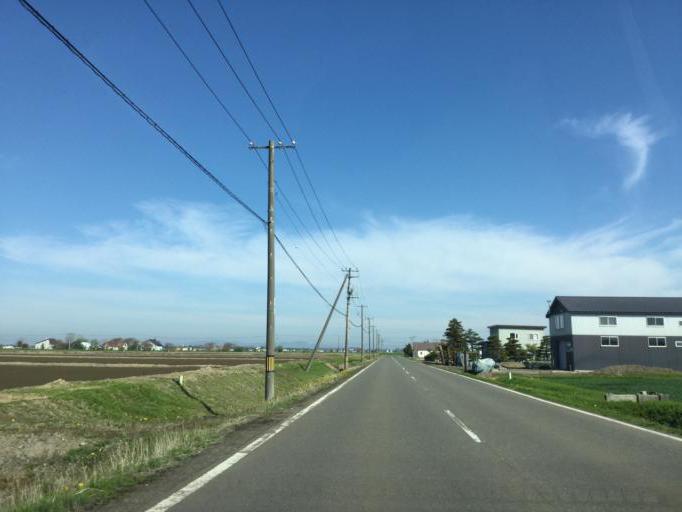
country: JP
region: Hokkaido
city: Iwamizawa
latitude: 43.1693
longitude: 141.7491
